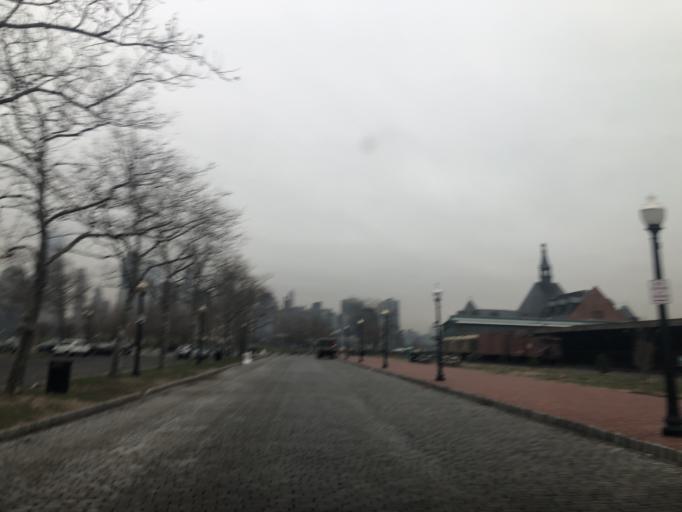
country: US
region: New York
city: New York City
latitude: 40.7082
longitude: -74.0371
